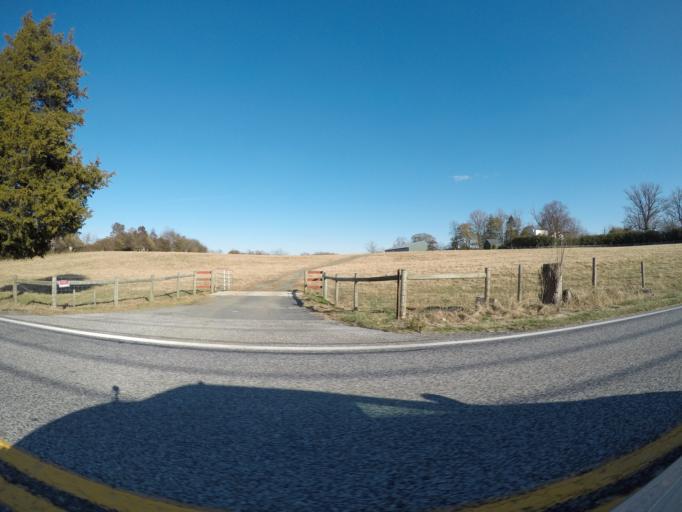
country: US
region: Maryland
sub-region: Harford County
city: Bel Air South
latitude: 39.5657
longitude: -76.2536
